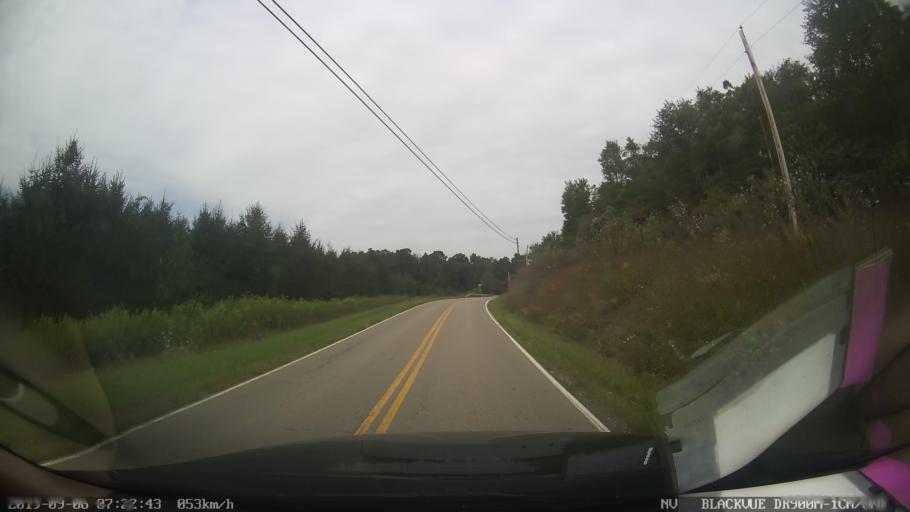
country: US
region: Ohio
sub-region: Licking County
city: Newark
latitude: 40.1411
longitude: -82.3775
